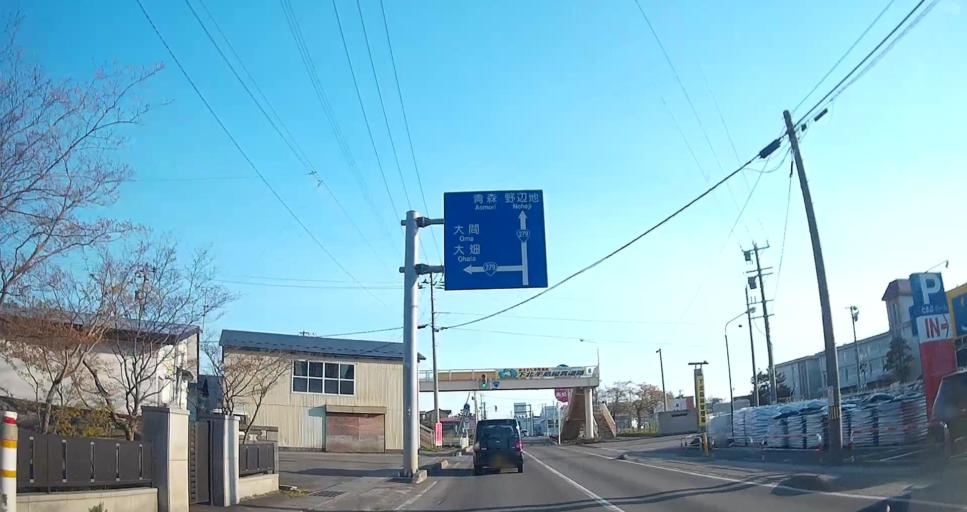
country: JP
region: Aomori
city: Mutsu
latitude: 41.2845
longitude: 141.2110
